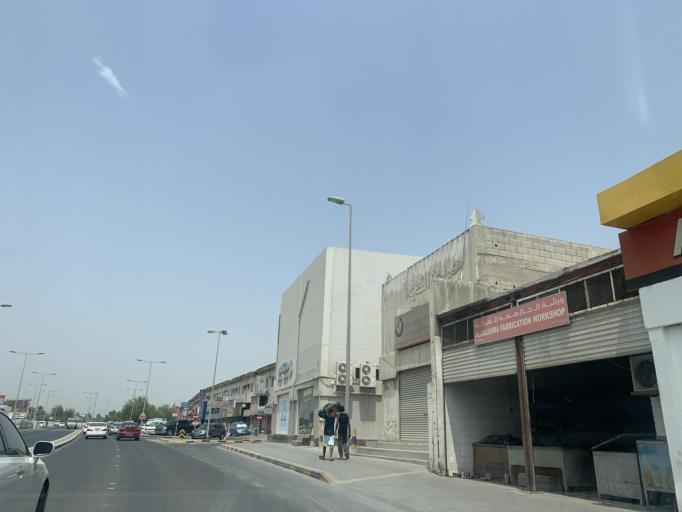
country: BH
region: Central Governorate
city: Madinat Hamad
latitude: 26.1419
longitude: 50.4910
